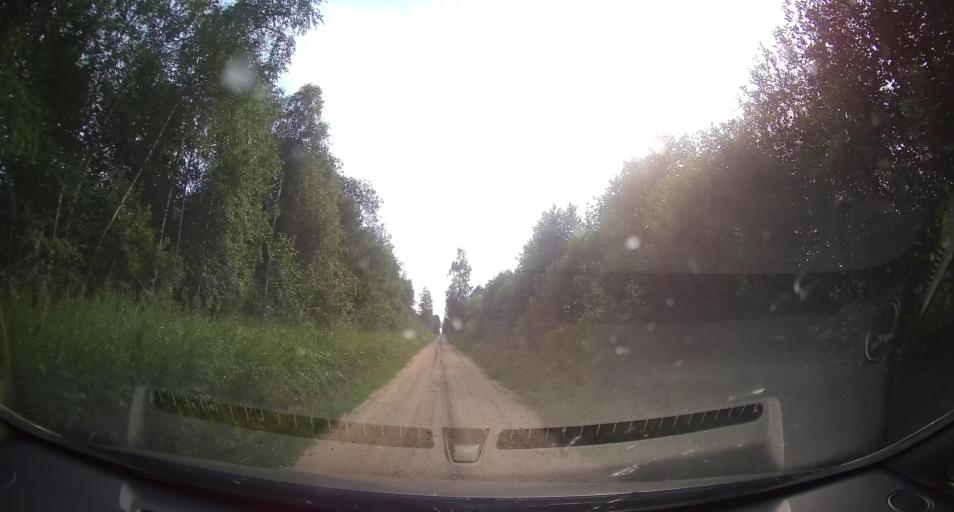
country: EE
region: Laeaene
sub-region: Lihula vald
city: Lihula
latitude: 58.6496
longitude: 23.7898
